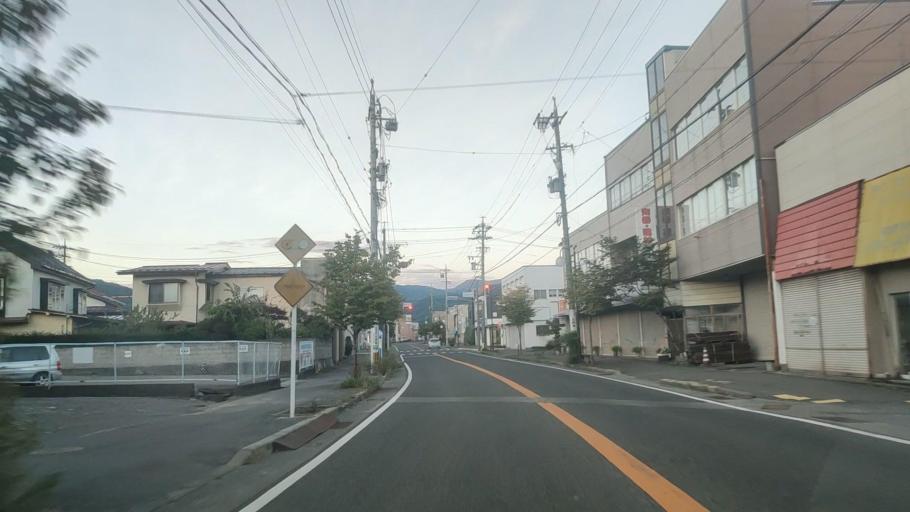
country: JP
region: Nagano
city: Okaya
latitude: 36.0701
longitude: 138.0592
